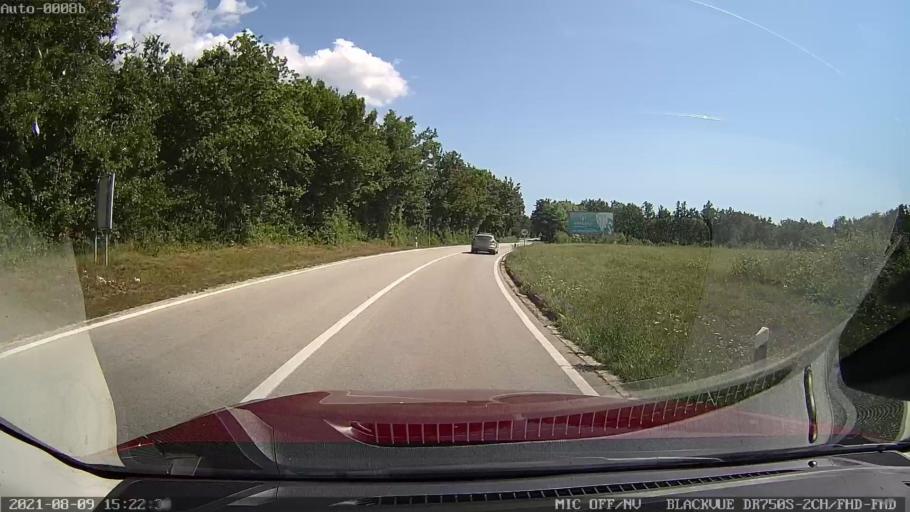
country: HR
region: Istarska
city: Pazin
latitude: 45.1907
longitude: 13.9016
